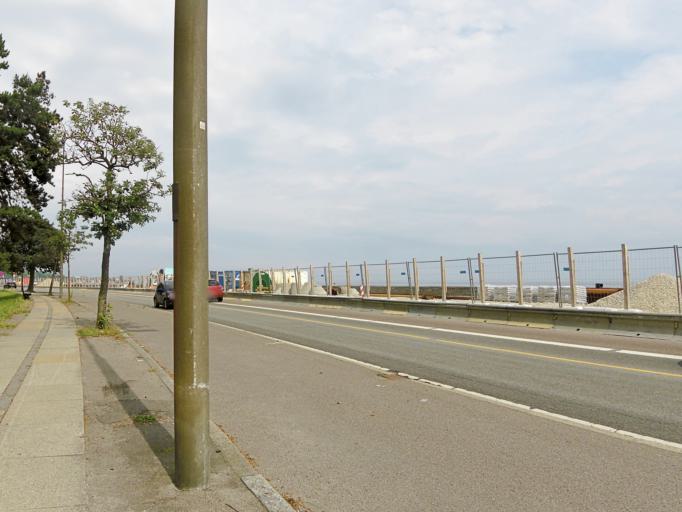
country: DK
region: Capital Region
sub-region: Gentofte Kommune
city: Charlottenlund
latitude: 55.7710
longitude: 12.5963
